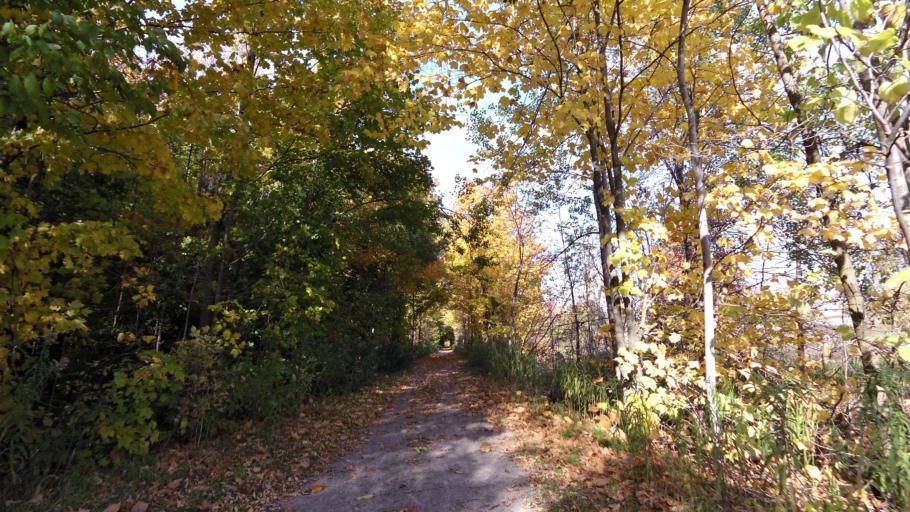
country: CA
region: Ontario
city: Orangeville
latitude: 43.8047
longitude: -80.0339
